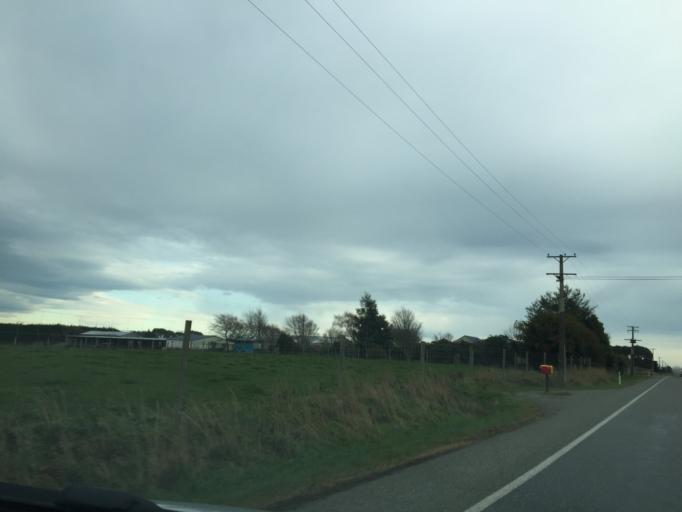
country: NZ
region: Southland
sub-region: Invercargill City
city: Invercargill
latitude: -46.3135
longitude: 168.6737
